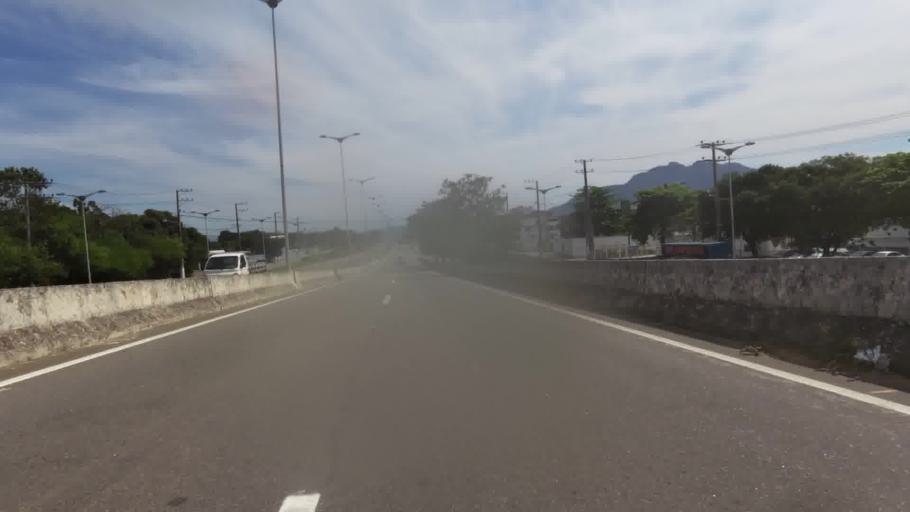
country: BR
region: Espirito Santo
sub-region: Vila Velha
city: Vila Velha
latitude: -20.2327
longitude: -40.2763
